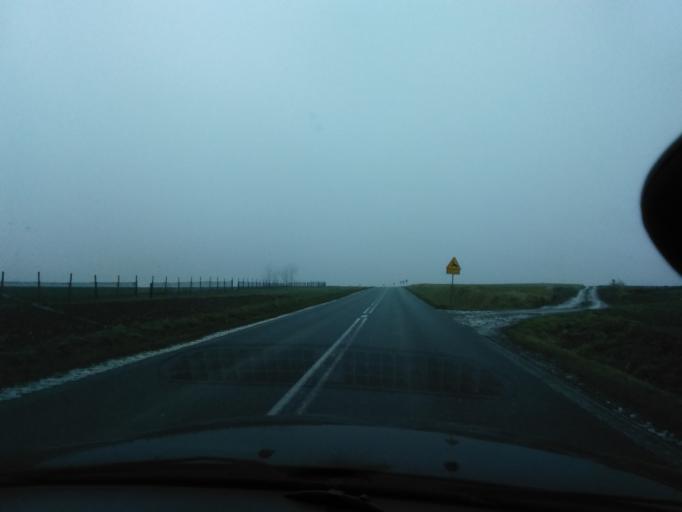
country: PL
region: Subcarpathian Voivodeship
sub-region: Powiat lancucki
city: Markowa
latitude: 50.0333
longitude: 22.3185
